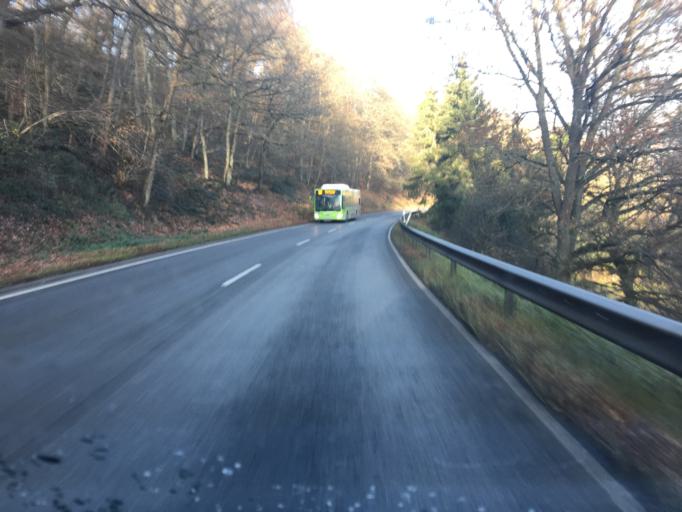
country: DE
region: North Rhine-Westphalia
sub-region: Regierungsbezirk Koln
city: Schleiden
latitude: 50.5691
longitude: 6.4866
